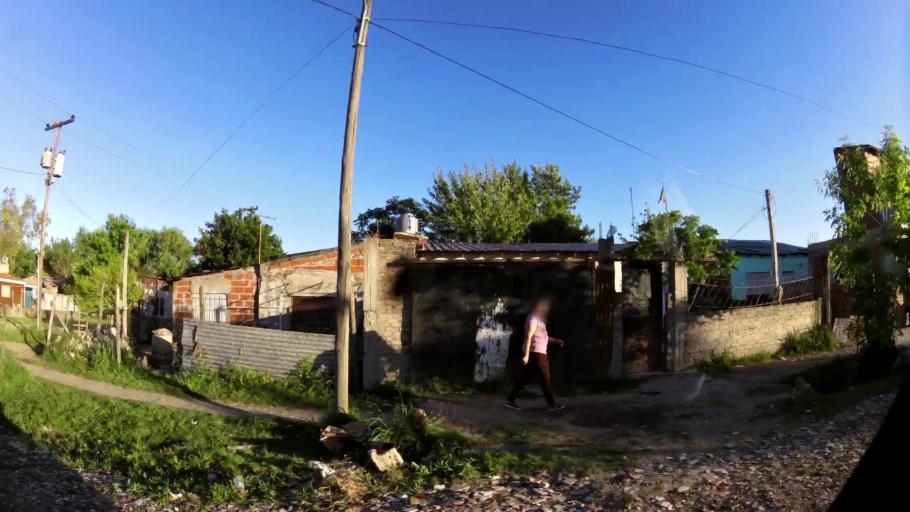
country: AR
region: Buenos Aires
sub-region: Partido de Almirante Brown
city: Adrogue
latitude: -34.7730
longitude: -58.3328
